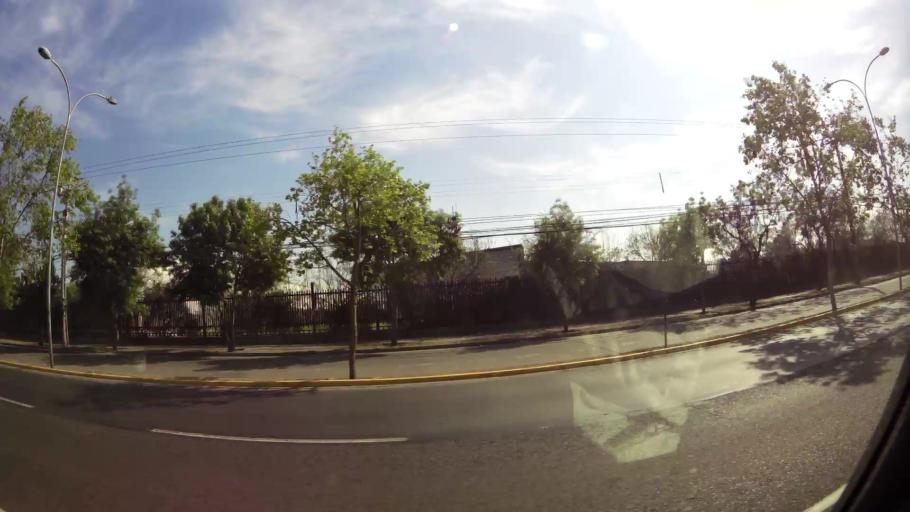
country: CL
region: Santiago Metropolitan
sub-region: Provincia de Santiago
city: Lo Prado
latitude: -33.4446
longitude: -70.7480
